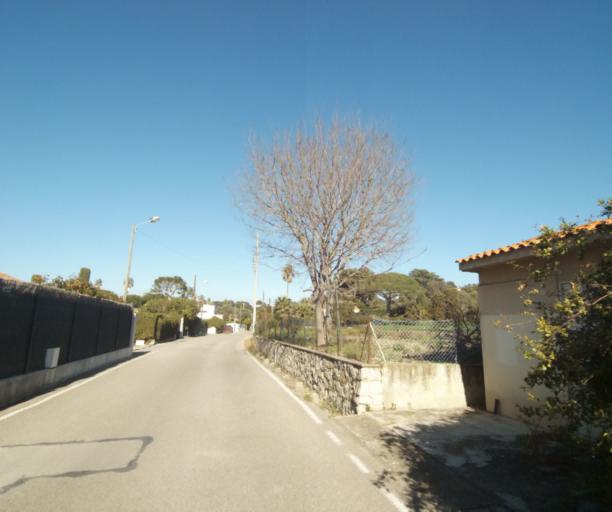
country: FR
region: Provence-Alpes-Cote d'Azur
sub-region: Departement des Alpes-Maritimes
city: Antibes
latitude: 43.5560
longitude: 7.1250
